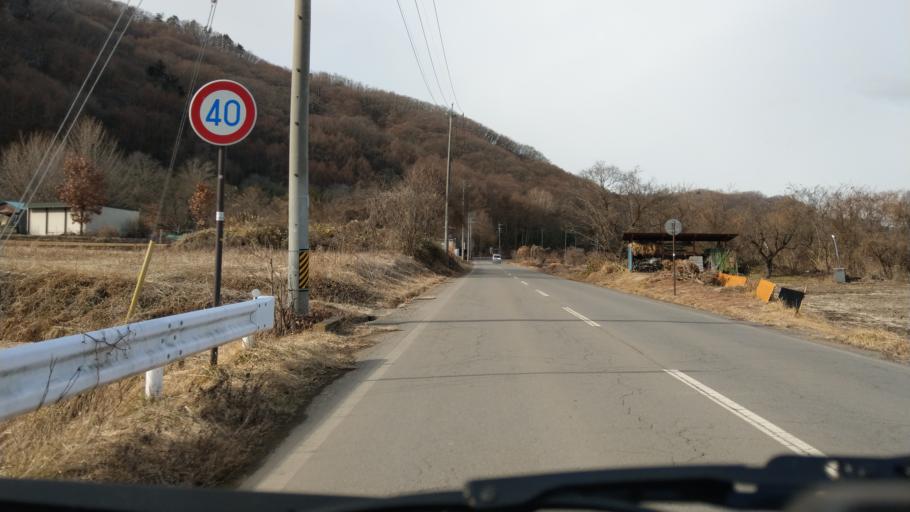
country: JP
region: Nagano
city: Komoro
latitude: 36.3352
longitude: 138.3697
